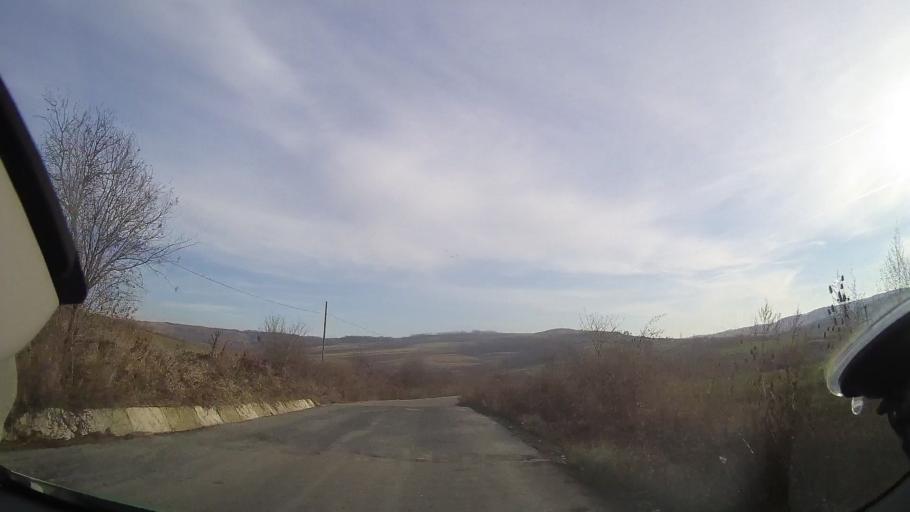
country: RO
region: Bihor
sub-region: Comuna Sarbi
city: Burzuc
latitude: 47.1710
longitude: 22.1577
